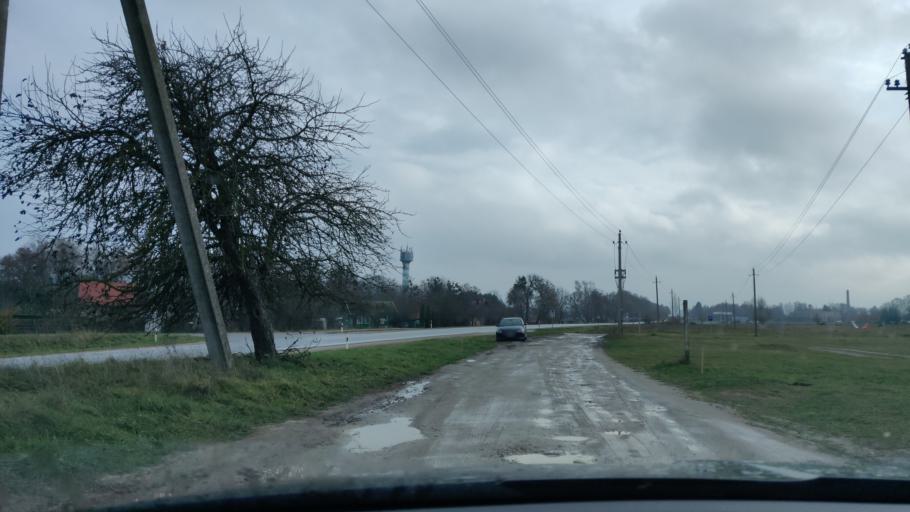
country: LT
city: Birstonas
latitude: 54.5994
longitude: 24.0234
